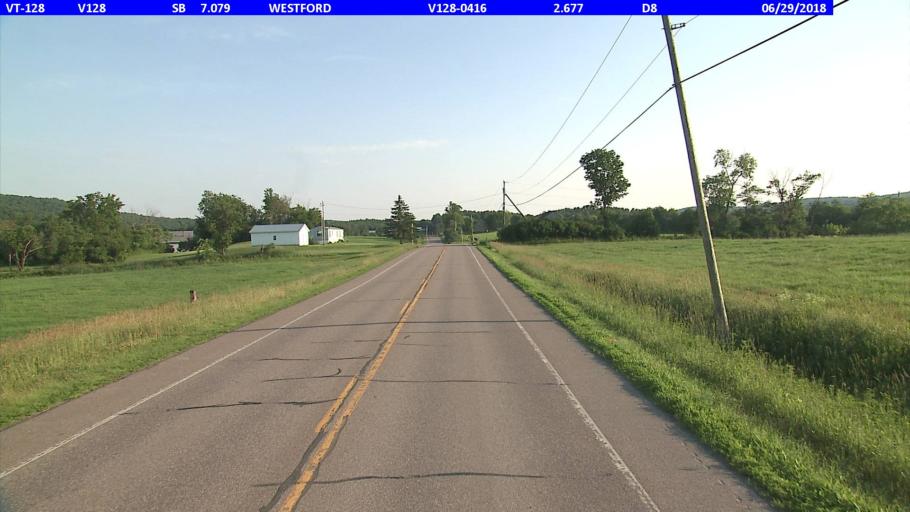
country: US
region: Vermont
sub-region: Chittenden County
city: Jericho
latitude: 44.5958
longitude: -73.0114
